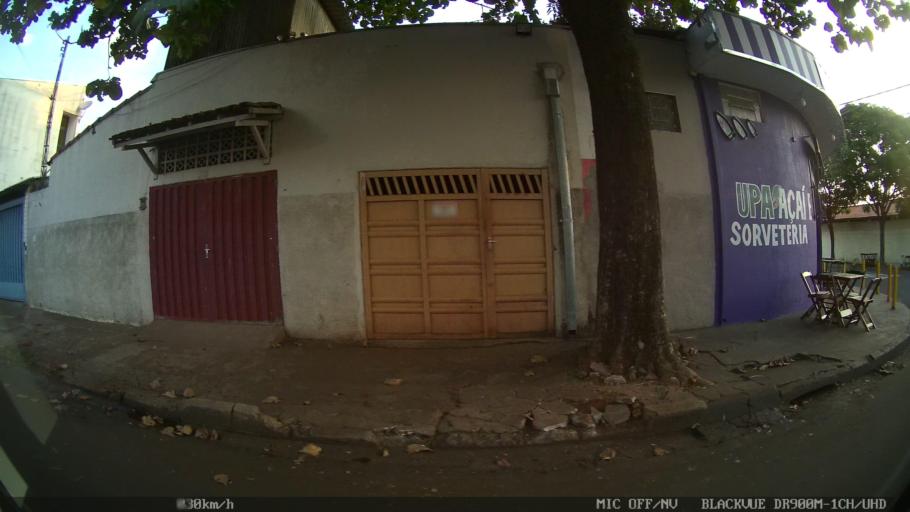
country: BR
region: Sao Paulo
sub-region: Ribeirao Preto
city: Ribeirao Preto
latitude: -21.1259
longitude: -47.8135
